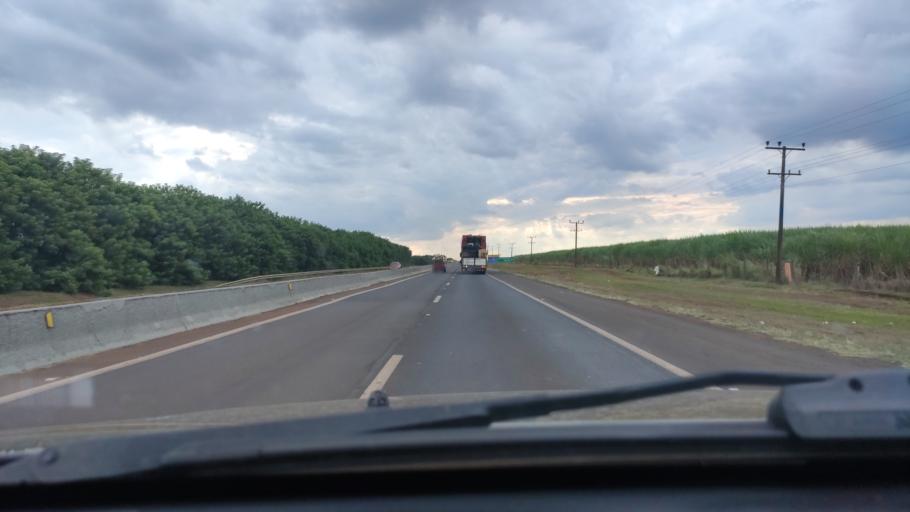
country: BR
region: Sao Paulo
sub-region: Palmital
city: Palmital
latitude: -22.7833
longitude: -50.1171
